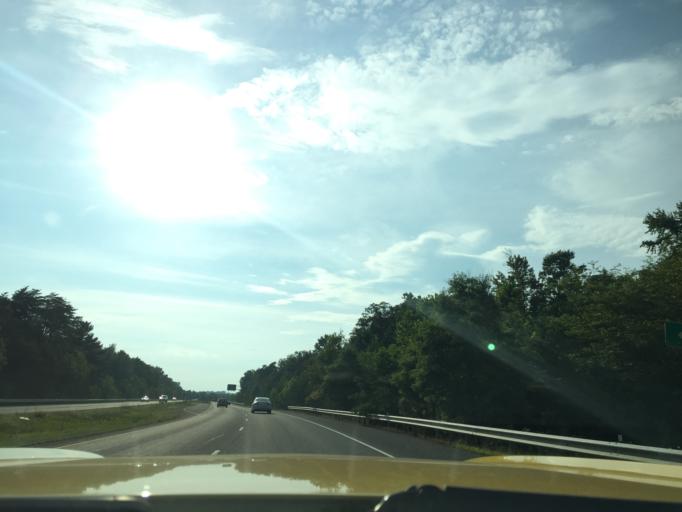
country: US
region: Virginia
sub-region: Fairfax County
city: Newington
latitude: 38.7213
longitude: -77.1734
